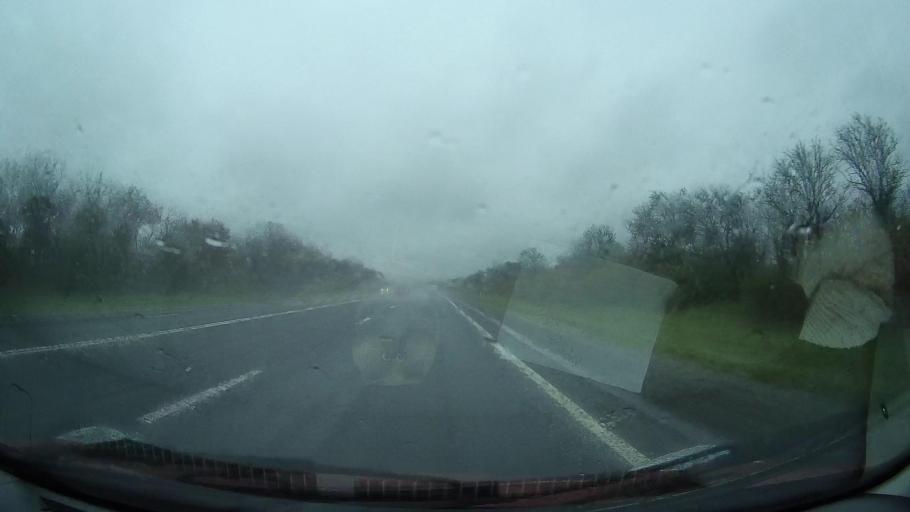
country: RU
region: Stavropol'skiy
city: Nevinnomyssk
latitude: 44.6186
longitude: 42.0969
